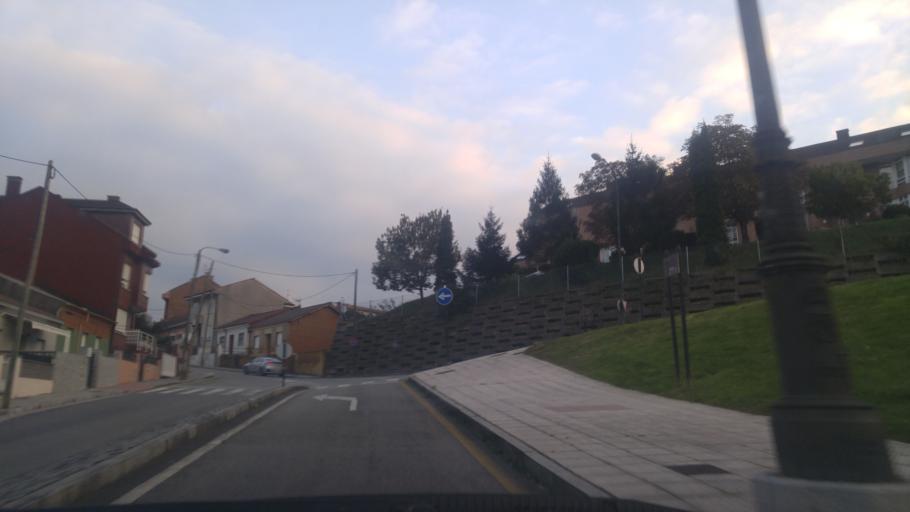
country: ES
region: Asturias
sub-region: Province of Asturias
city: Oviedo
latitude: 43.3733
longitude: -5.8584
